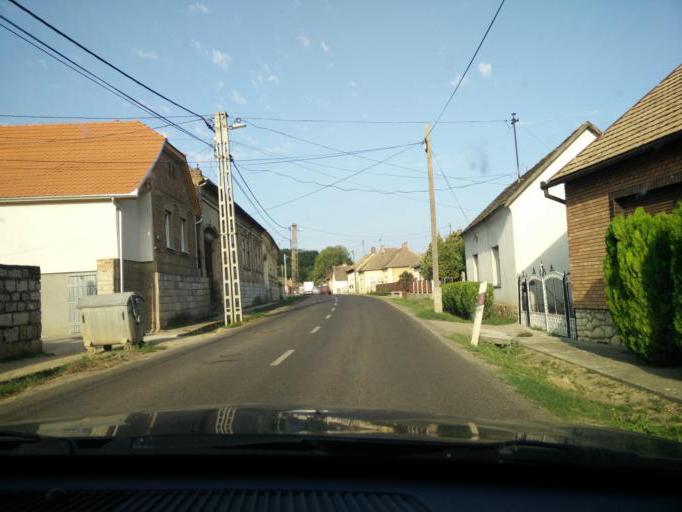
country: HU
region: Baranya
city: Szaszvar
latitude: 46.2721
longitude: 18.3871
